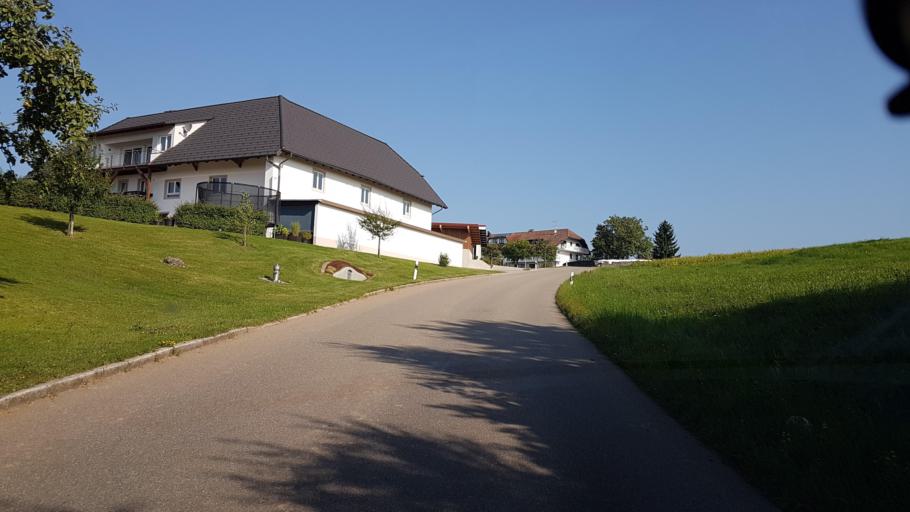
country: DE
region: Baden-Wuerttemberg
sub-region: Freiburg Region
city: Gorwihl
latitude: 47.6204
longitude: 8.1033
